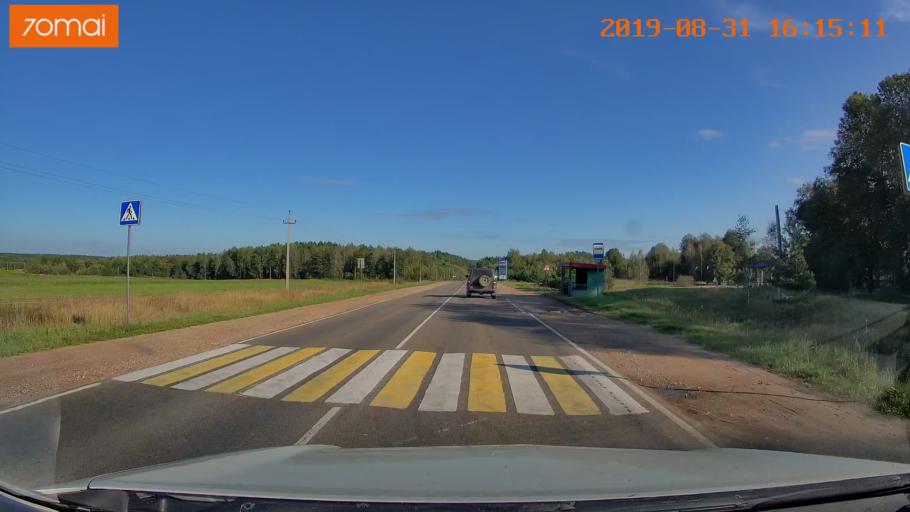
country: RU
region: Kaluga
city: Nikola-Lenivets
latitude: 54.5615
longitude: 35.4831
